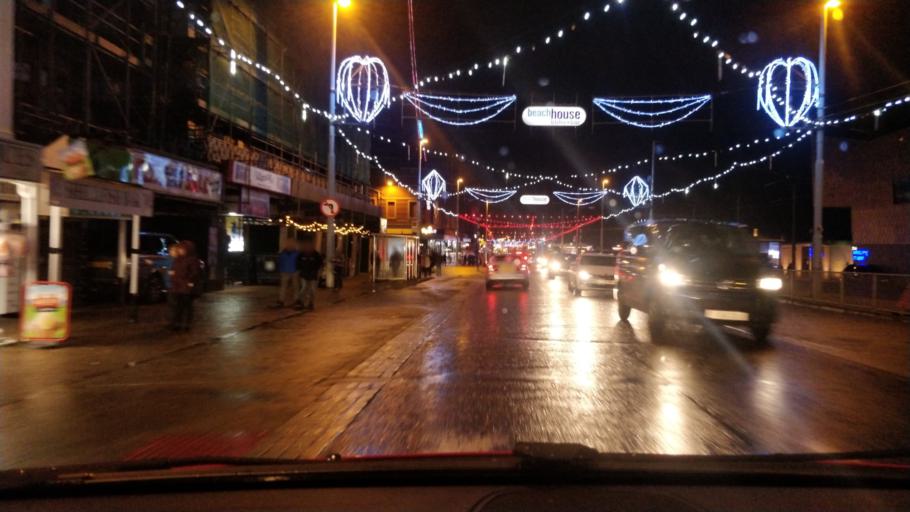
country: GB
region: England
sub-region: Blackpool
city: Blackpool
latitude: 53.8181
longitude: -3.0558
